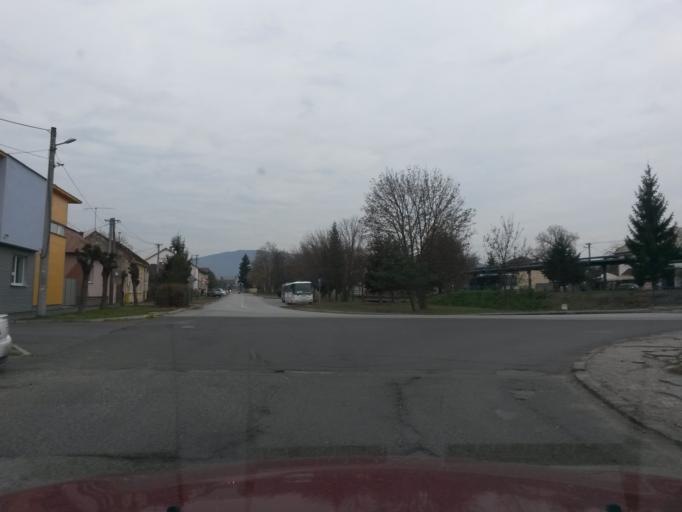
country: SK
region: Kosicky
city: Secovce
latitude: 48.7006
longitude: 21.6550
